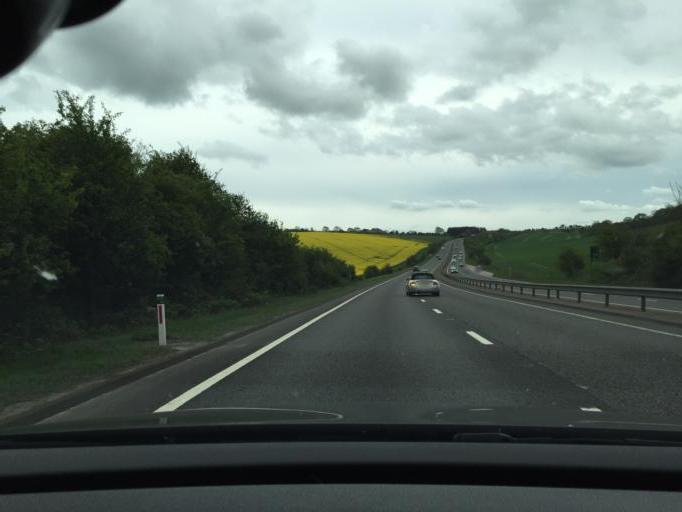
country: GB
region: England
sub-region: West Berkshire
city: Hermitage
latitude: 51.5206
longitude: -1.2913
